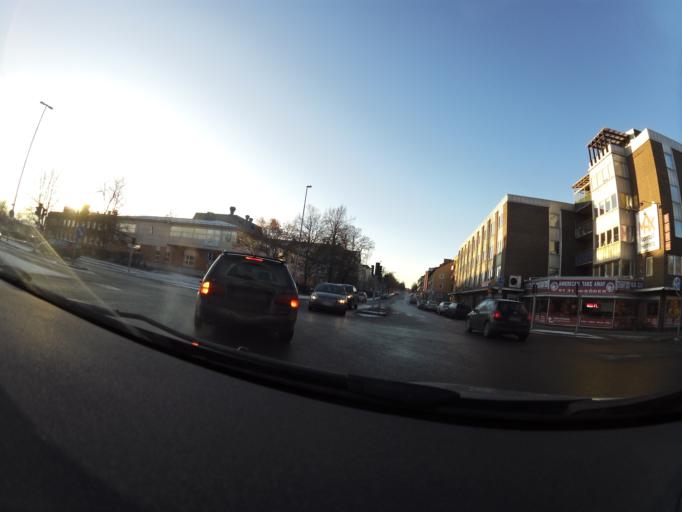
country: SE
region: Gaevleborg
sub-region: Gavle Kommun
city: Gavle
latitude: 60.6676
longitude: 17.1519
